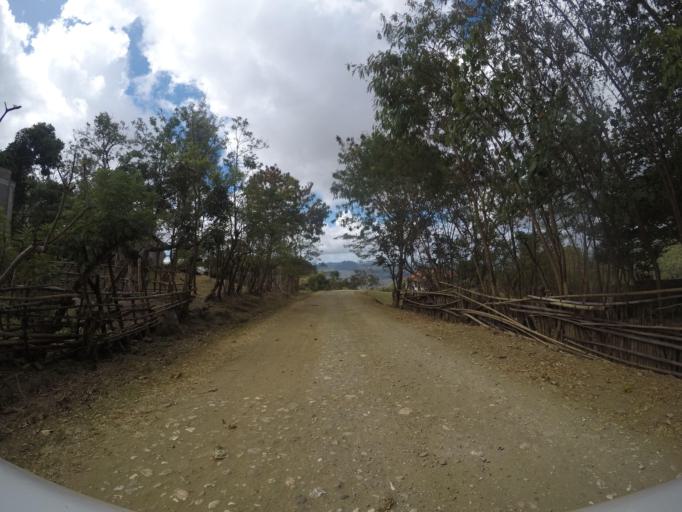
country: TL
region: Lautem
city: Lospalos
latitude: -8.5448
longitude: 126.8357
